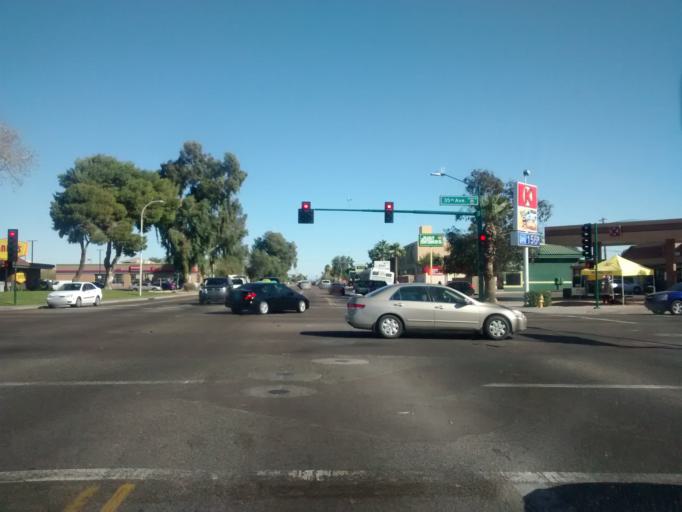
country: US
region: Arizona
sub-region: Maricopa County
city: Glendale
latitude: 33.5240
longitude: -112.1345
